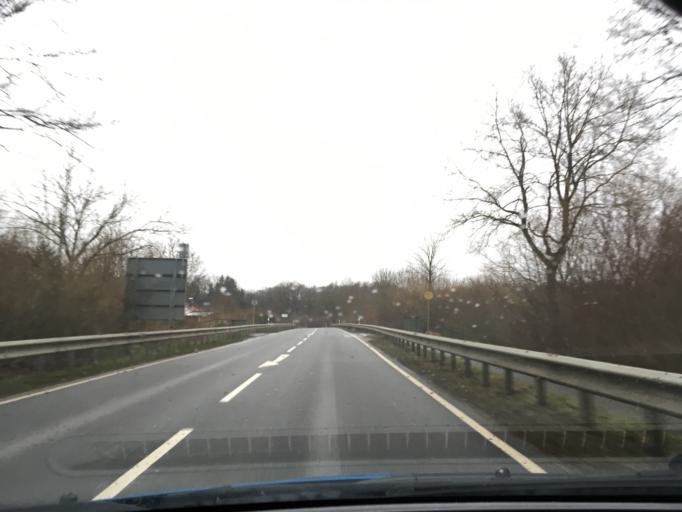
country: DE
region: Schleswig-Holstein
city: Hornbek
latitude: 53.5600
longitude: 10.6483
